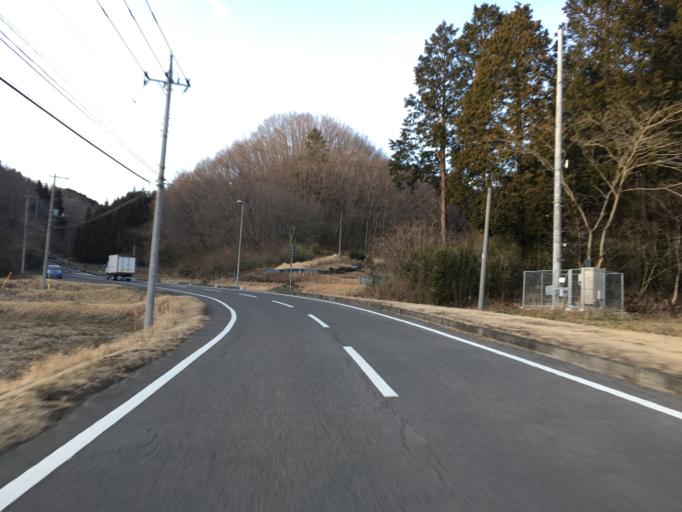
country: JP
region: Ibaraki
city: Daigo
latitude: 36.7787
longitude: 140.4268
